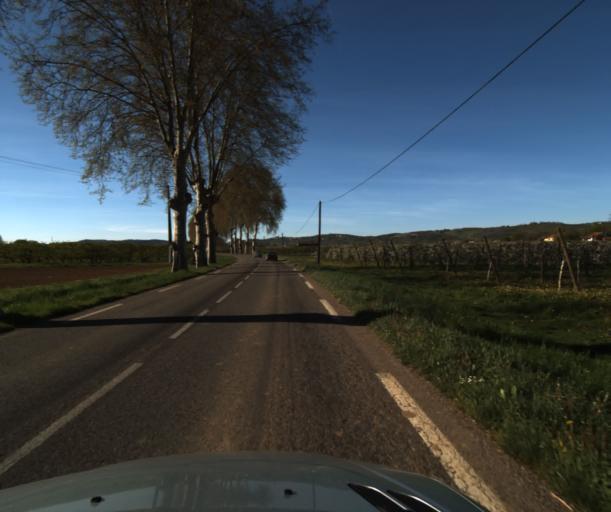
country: FR
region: Midi-Pyrenees
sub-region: Departement du Tarn-et-Garonne
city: Lafrancaise
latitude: 44.0917
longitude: 1.2651
